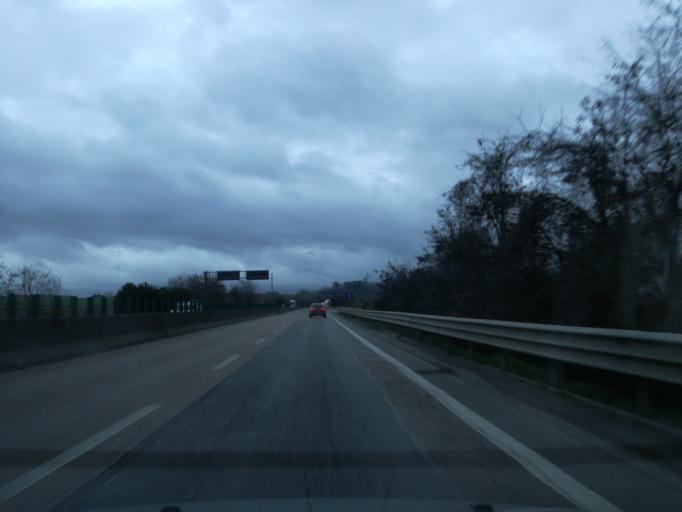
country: IT
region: Umbria
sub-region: Provincia di Perugia
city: Via Lippia
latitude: 43.0992
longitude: 12.4762
